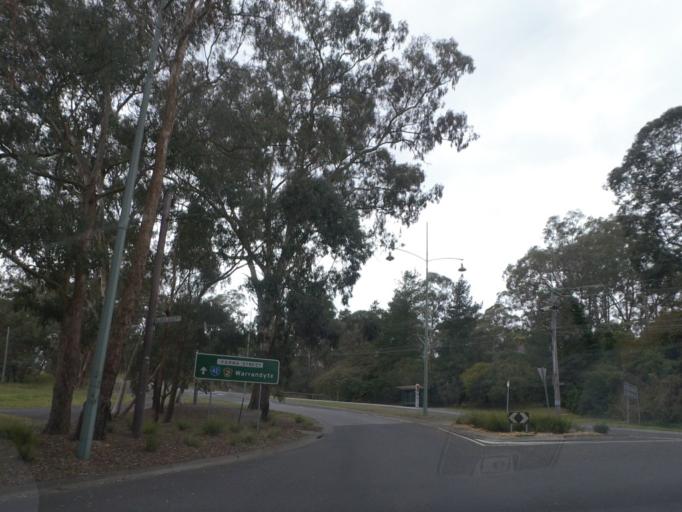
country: AU
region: Victoria
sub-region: Nillumbik
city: North Warrandyte
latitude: -37.7473
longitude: 145.2098
